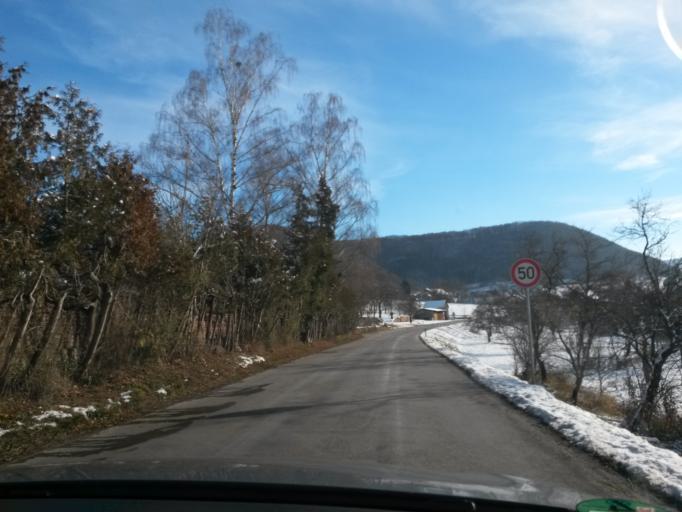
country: DE
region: Baden-Wuerttemberg
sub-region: Regierungsbezirk Stuttgart
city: Gingen an der Fils
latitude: 48.6325
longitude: 9.7601
